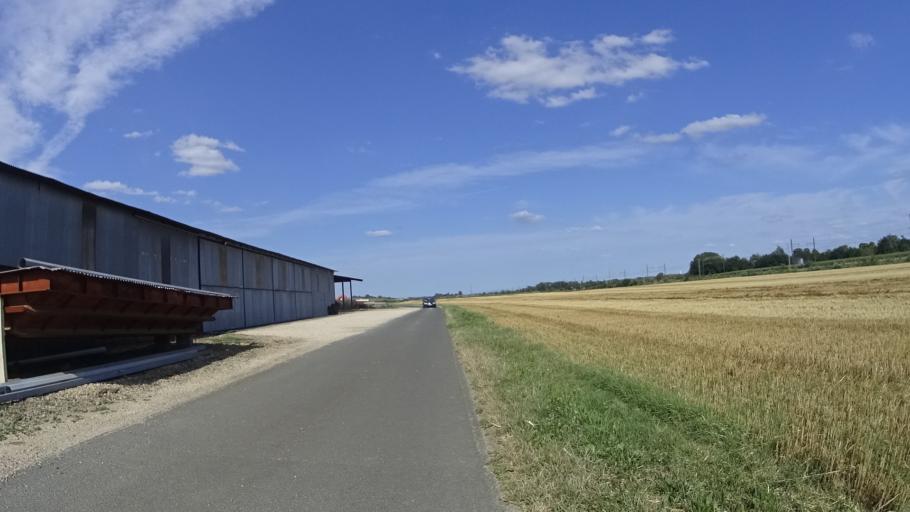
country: FR
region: Centre
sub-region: Departement d'Indre-et-Loire
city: Cangey
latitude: 47.4695
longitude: 1.0960
